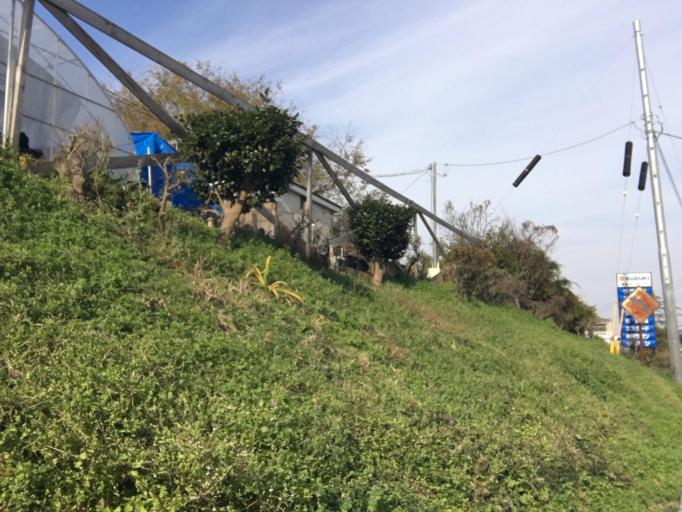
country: JP
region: Saitama
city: Yorii
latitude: 36.1405
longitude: 139.1998
